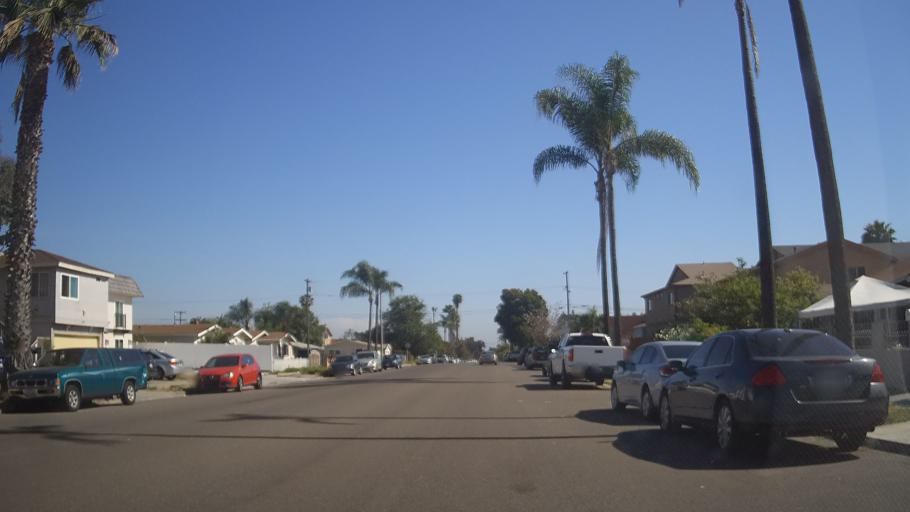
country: US
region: California
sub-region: San Diego County
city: San Diego
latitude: 32.7468
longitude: -117.1058
